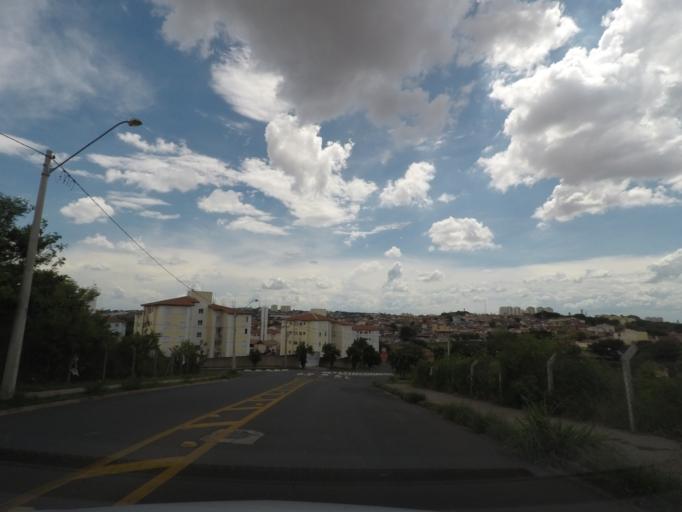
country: BR
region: Sao Paulo
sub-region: Campinas
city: Campinas
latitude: -22.9247
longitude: -47.0176
